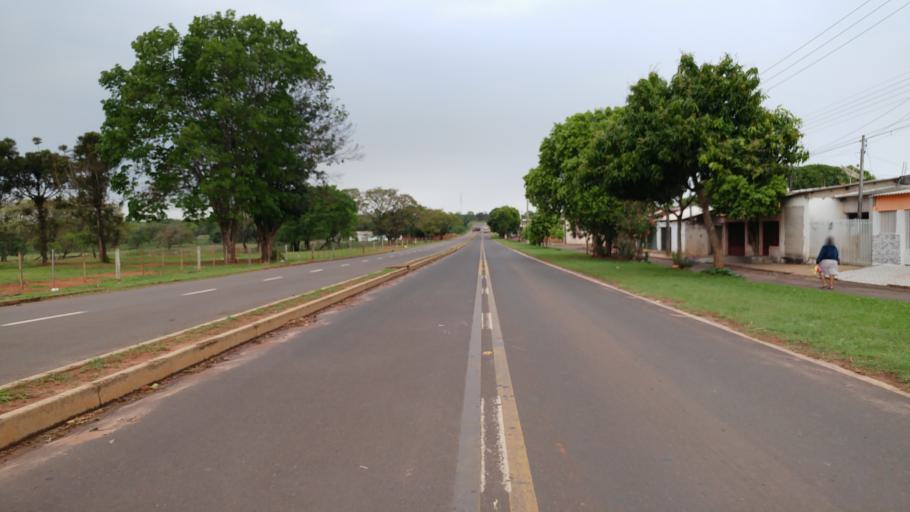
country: BR
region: Sao Paulo
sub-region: Paraguacu Paulista
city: Paraguacu Paulista
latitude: -22.4382
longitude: -50.5810
